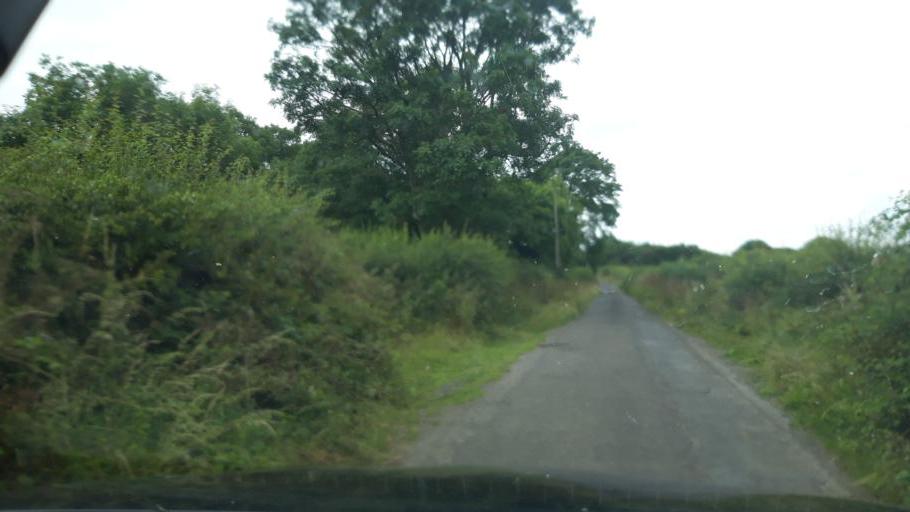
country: IE
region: Leinster
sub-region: Kilkenny
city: Graiguenamanagh
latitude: 52.5989
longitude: -7.0348
